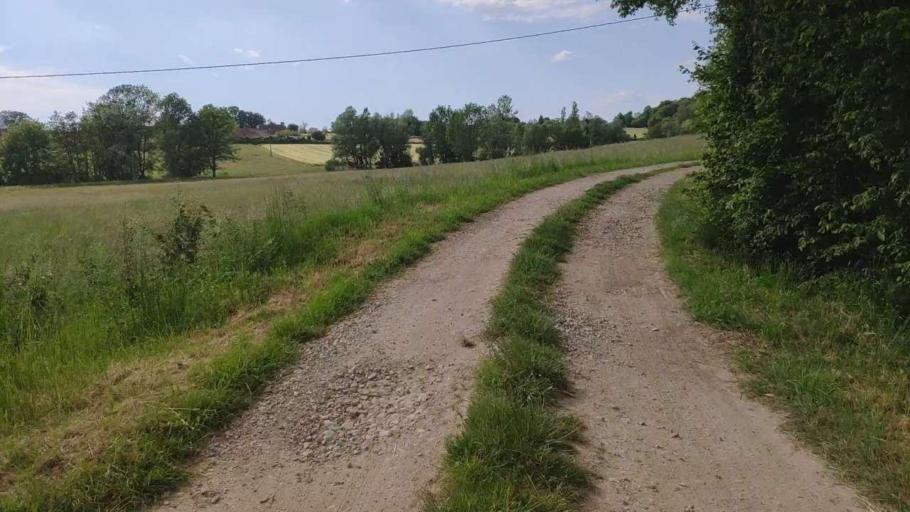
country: FR
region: Bourgogne
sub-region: Departement de Saone-et-Loire
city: Saint-Germain-du-Bois
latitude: 46.8047
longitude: 5.3445
